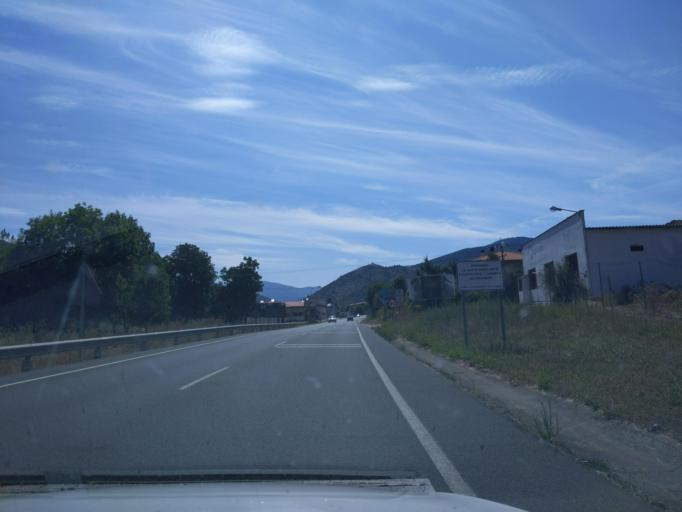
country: ES
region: La Rioja
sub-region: Provincia de La Rioja
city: Ojacastro
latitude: 42.3371
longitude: -3.0104
